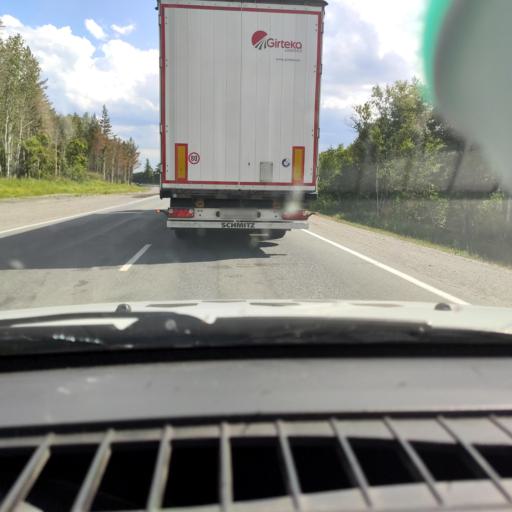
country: RU
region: Chelyabinsk
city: Zlatoust
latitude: 55.0275
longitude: 59.7230
